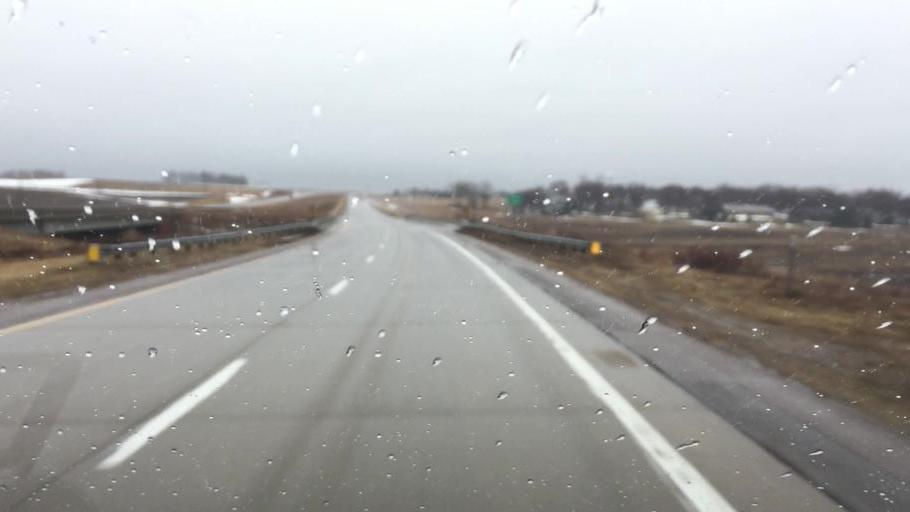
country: US
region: Iowa
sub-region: O'Brien County
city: Sheldon
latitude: 43.0809
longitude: -95.9005
